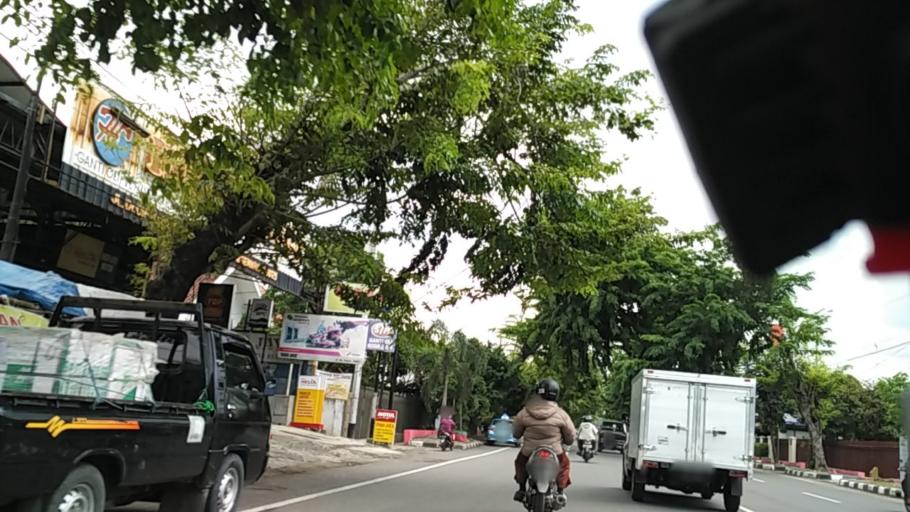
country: ID
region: Central Java
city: Semarang
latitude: -6.9905
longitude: 110.4344
